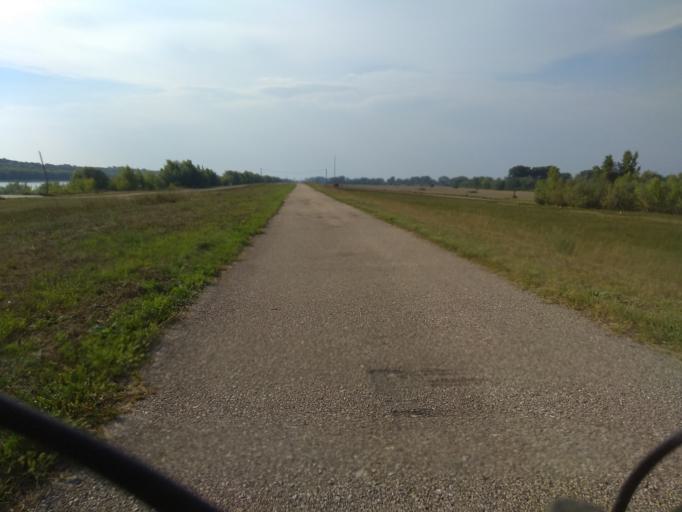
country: SK
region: Trnavsky
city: Gabcikovo
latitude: 47.8237
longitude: 17.6094
